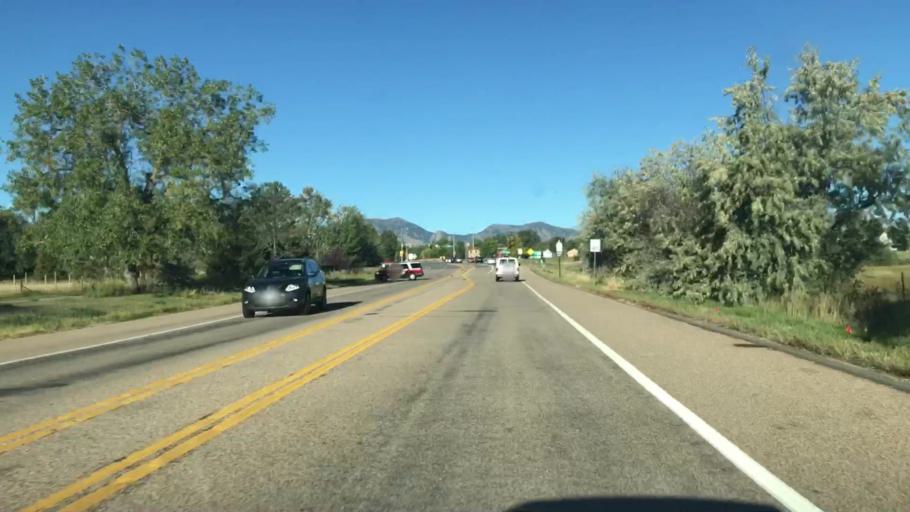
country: US
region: Colorado
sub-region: Boulder County
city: Louisville
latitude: 39.9726
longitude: -105.1236
